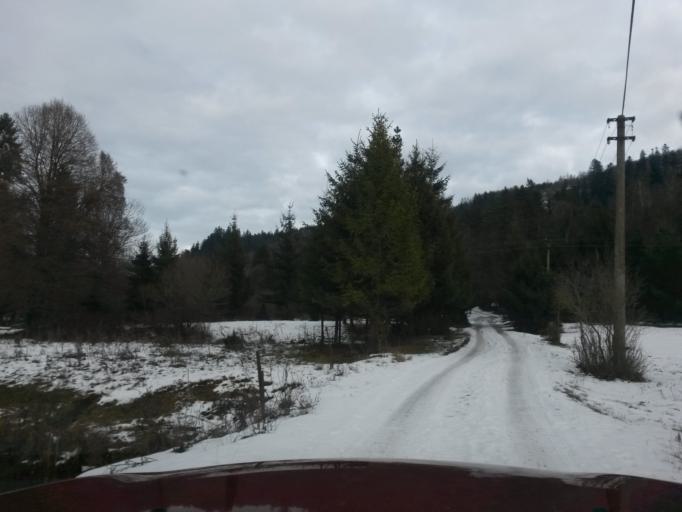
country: SK
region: Kosicky
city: Spisska Nova Ves
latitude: 48.8836
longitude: 20.5955
